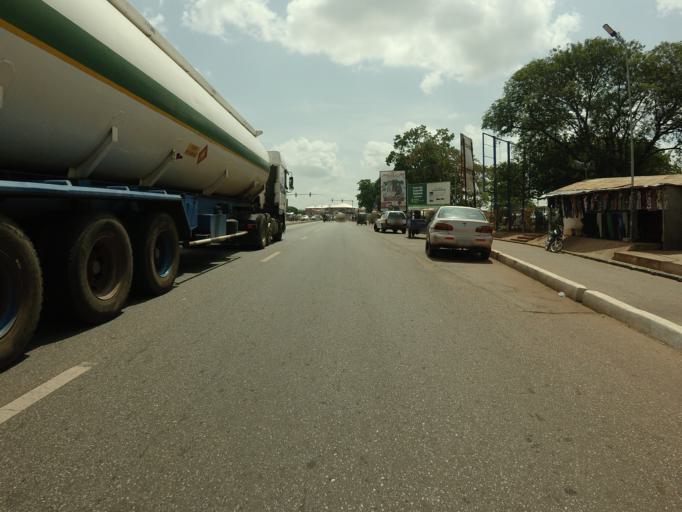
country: GH
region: Northern
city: Tamale
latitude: 9.4015
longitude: -0.8376
